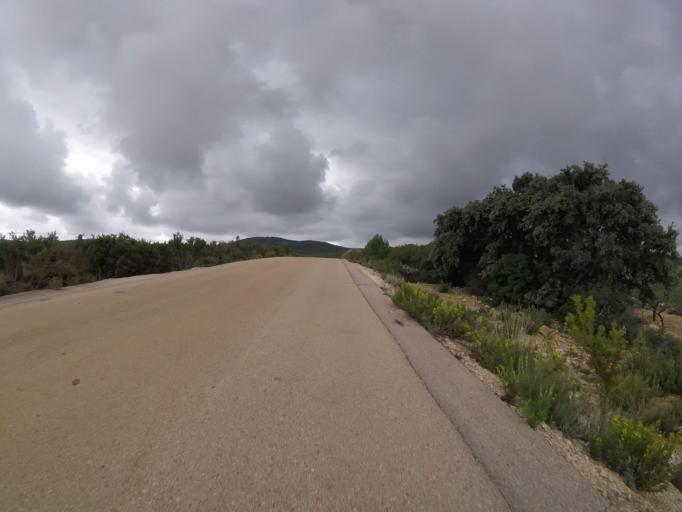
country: ES
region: Valencia
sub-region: Provincia de Castello
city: Benlloch
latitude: 40.2029
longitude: 0.0650
